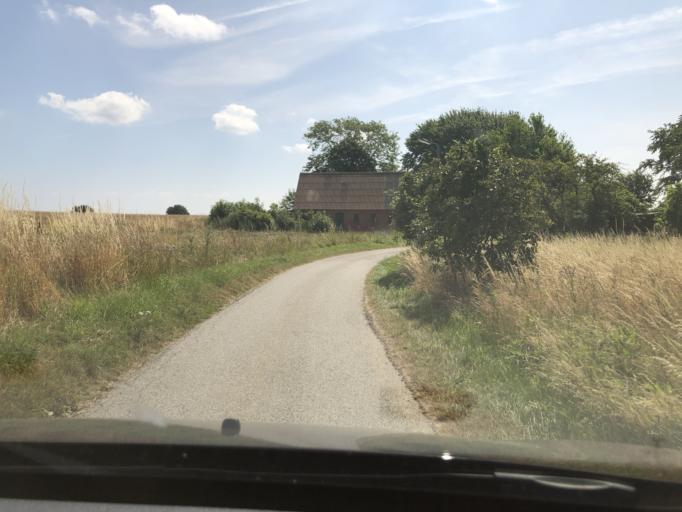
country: DK
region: South Denmark
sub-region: AEro Kommune
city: AEroskobing
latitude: 54.9140
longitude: 10.3217
